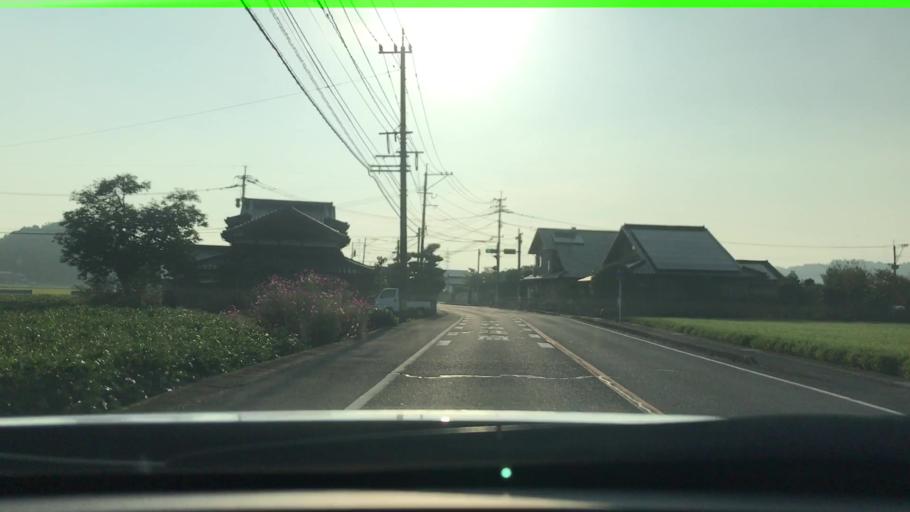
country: JP
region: Saga Prefecture
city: Takeocho-takeo
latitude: 33.2086
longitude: 130.0754
